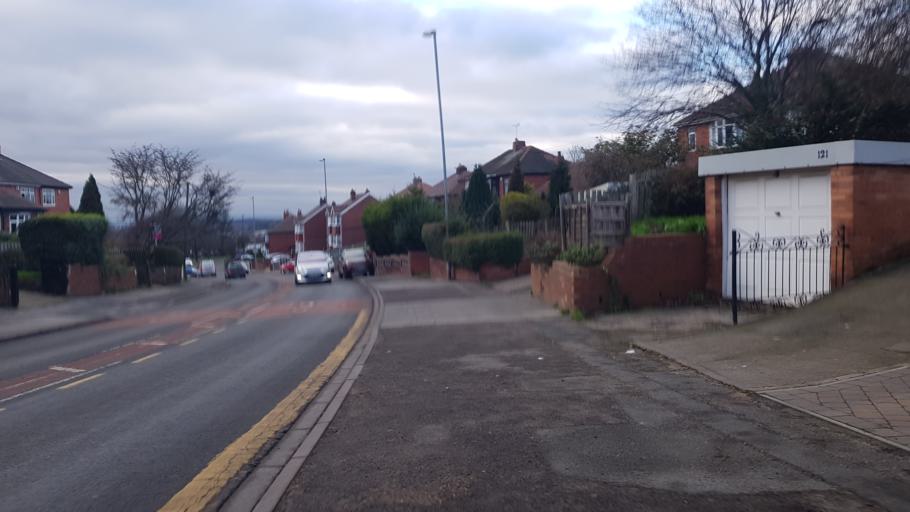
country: GB
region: England
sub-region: City and Borough of Wakefield
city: Pontefract
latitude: 53.7165
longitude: -1.3280
